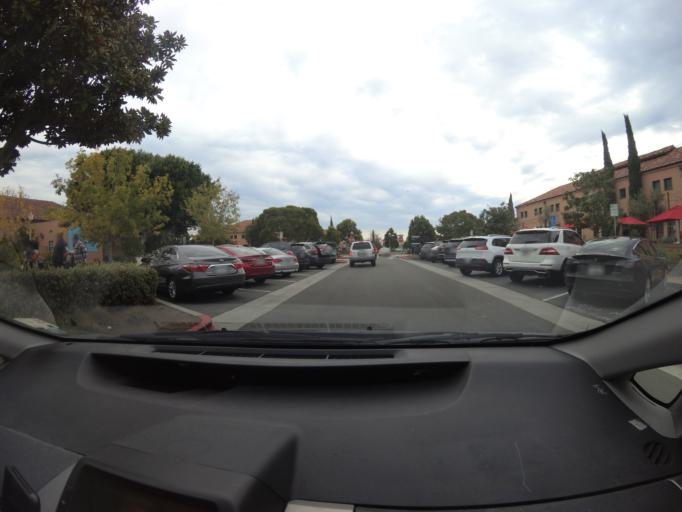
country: US
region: California
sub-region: San Diego County
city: San Diego
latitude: 32.7407
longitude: -117.2111
